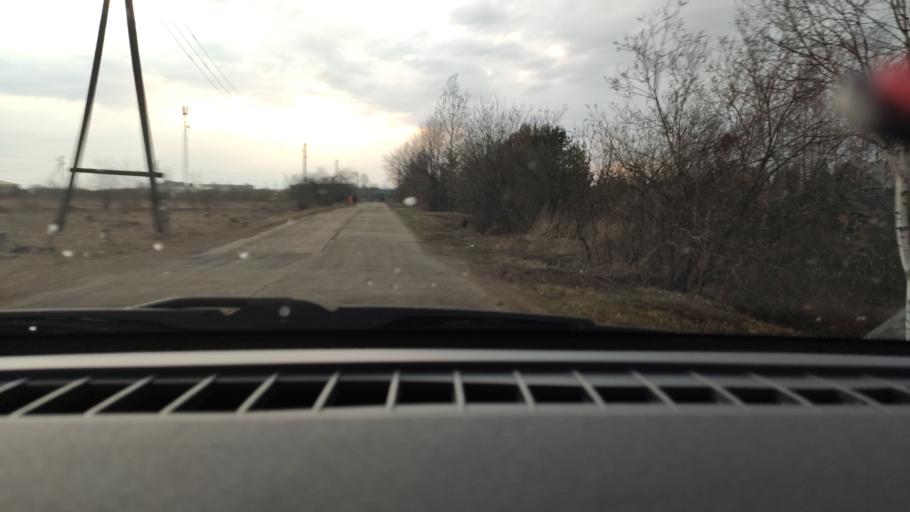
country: RU
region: Perm
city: Gamovo
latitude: 57.8746
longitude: 56.0956
